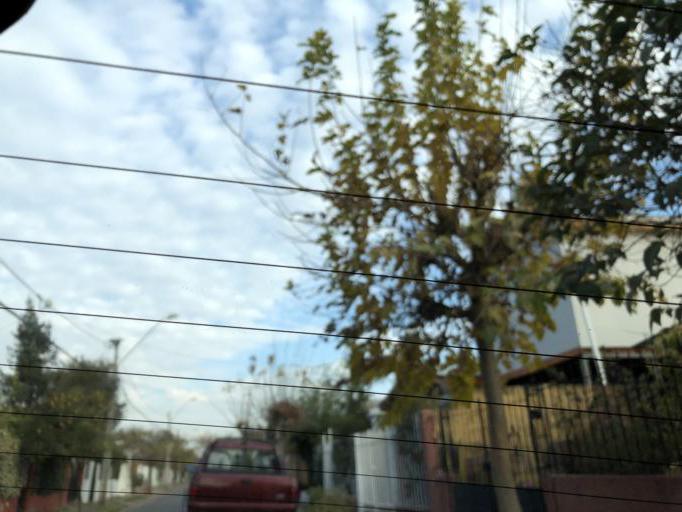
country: CL
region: Santiago Metropolitan
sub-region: Provincia de Cordillera
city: Puente Alto
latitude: -33.6039
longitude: -70.5667
